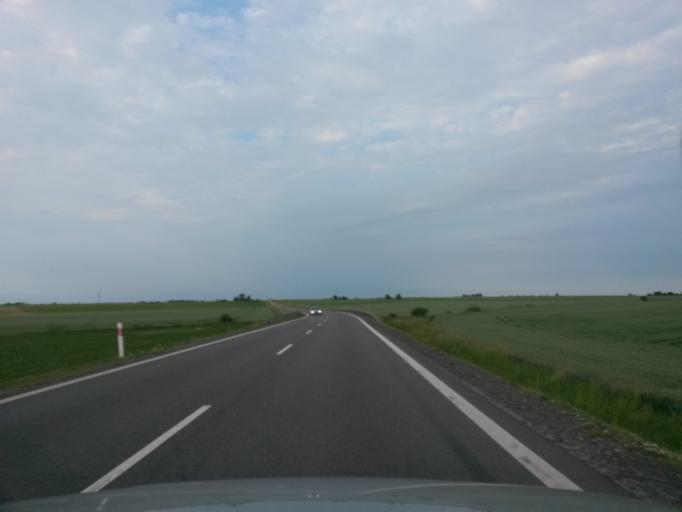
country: PL
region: Lower Silesian Voivodeship
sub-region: Powiat swidnicki
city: Zarow
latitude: 51.0199
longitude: 16.5679
